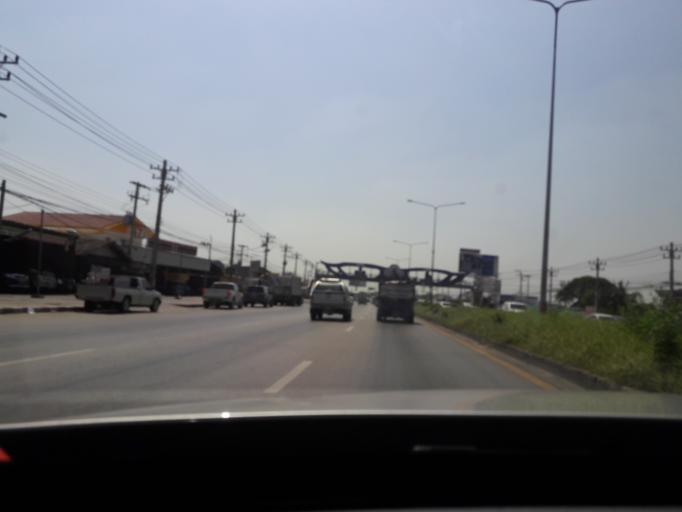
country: TH
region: Bangkok
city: Nong Khaem
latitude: 13.6816
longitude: 100.3217
